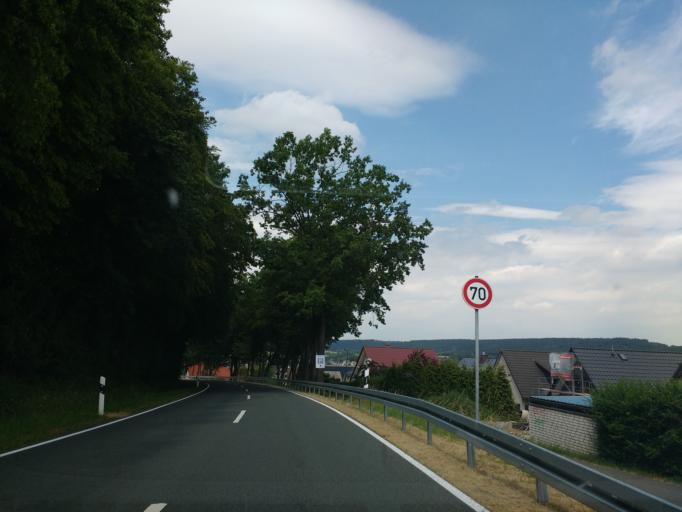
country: DE
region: North Rhine-Westphalia
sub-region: Regierungsbezirk Detmold
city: Altenbeken
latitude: 51.7496
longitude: 8.9468
